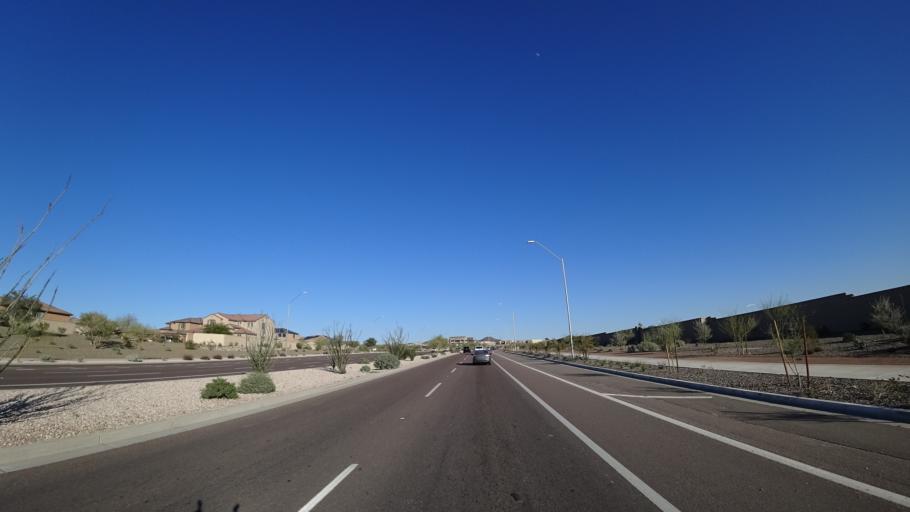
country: US
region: Arizona
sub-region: Maricopa County
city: Sun City West
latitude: 33.7137
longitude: -112.2844
